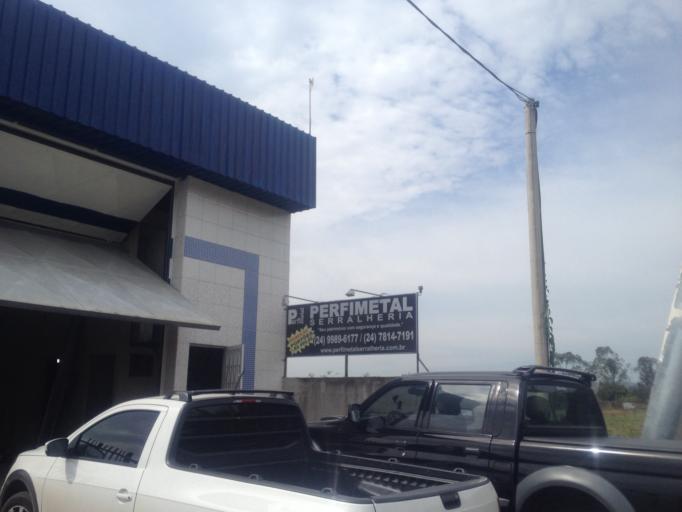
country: BR
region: Rio de Janeiro
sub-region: Porto Real
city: Porto Real
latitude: -22.4307
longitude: -44.3176
